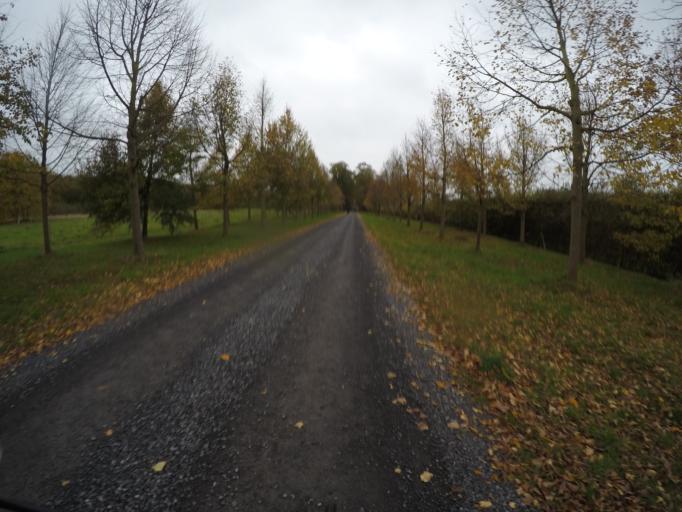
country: BE
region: Flanders
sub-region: Provincie Antwerpen
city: Wijnegem
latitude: 51.2262
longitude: 4.4900
